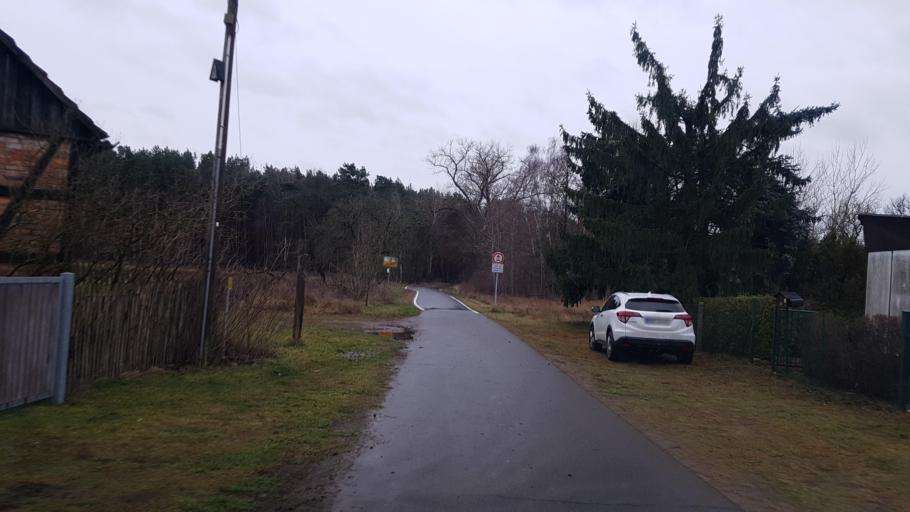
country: DE
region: Brandenburg
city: Tauche
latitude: 52.1031
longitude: 14.1184
